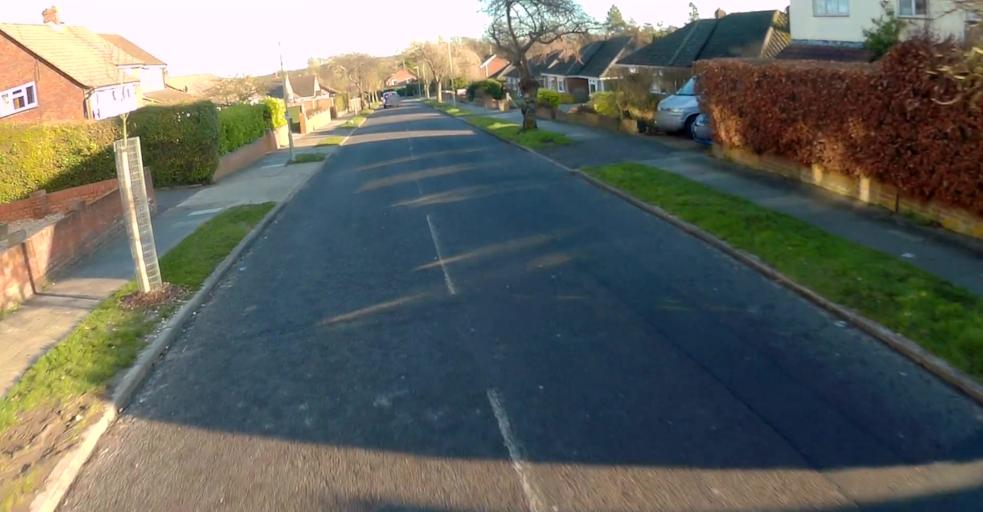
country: GB
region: England
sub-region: Hampshire
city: Basingstoke
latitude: 51.2514
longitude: -1.0909
